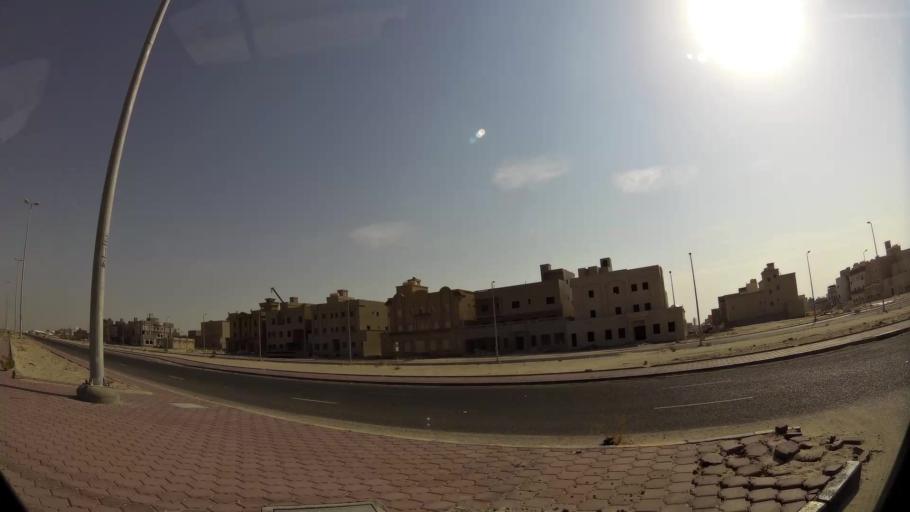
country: KW
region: Al Ahmadi
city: Al Wafrah
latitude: 28.7809
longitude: 48.0323
